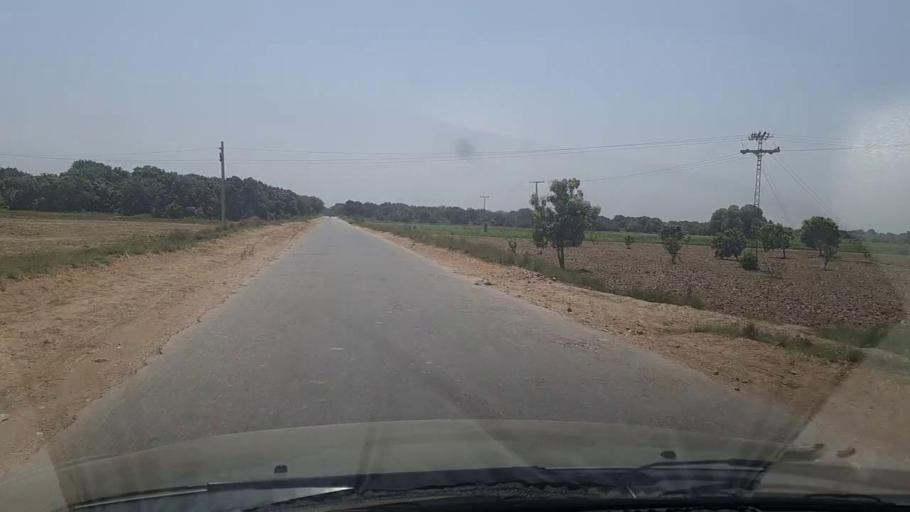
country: PK
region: Sindh
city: Tando Jam
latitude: 25.2939
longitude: 68.5883
